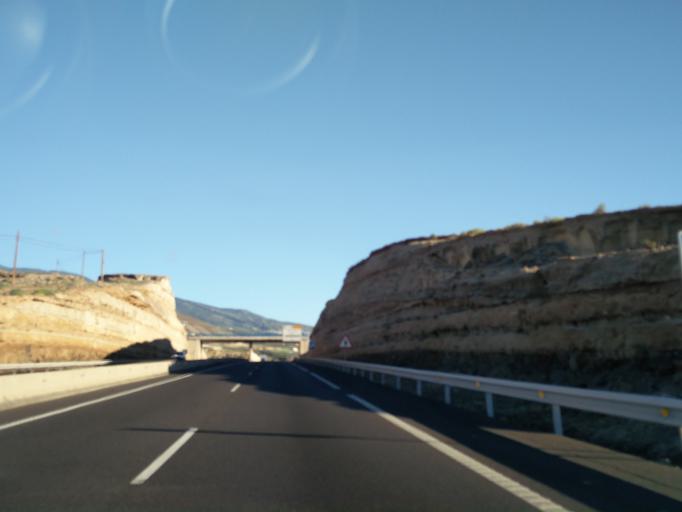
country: ES
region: Canary Islands
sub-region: Provincia de Santa Cruz de Tenerife
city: Fasnia
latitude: 28.1987
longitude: -16.4262
